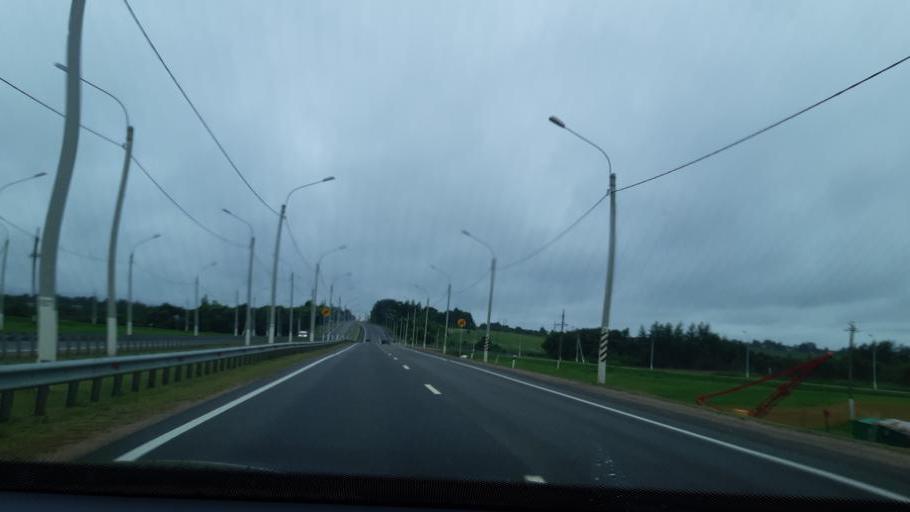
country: RU
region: Smolensk
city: Talashkino
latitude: 54.7068
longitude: 32.1169
